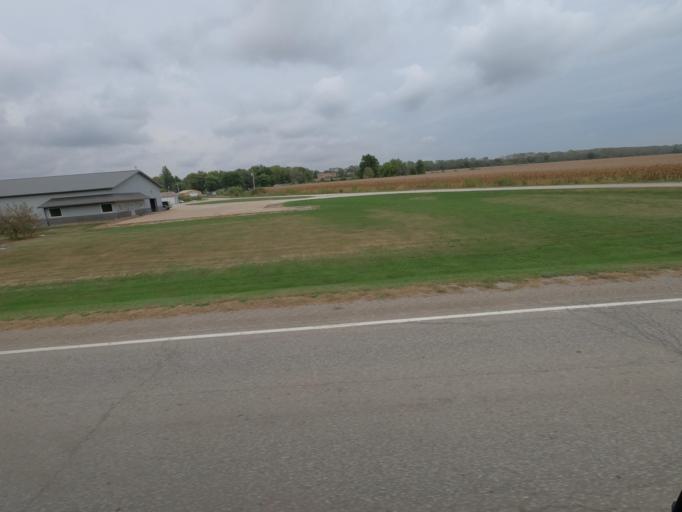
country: US
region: Iowa
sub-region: Wapello County
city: Ottumwa
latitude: 40.9128
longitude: -92.2134
